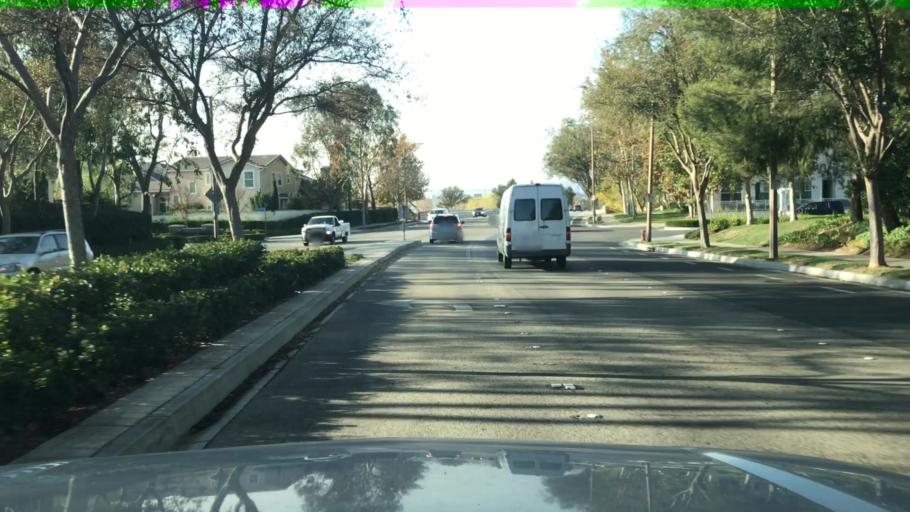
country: US
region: California
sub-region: Los Angeles County
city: Santa Clarita
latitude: 34.4283
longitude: -118.5626
